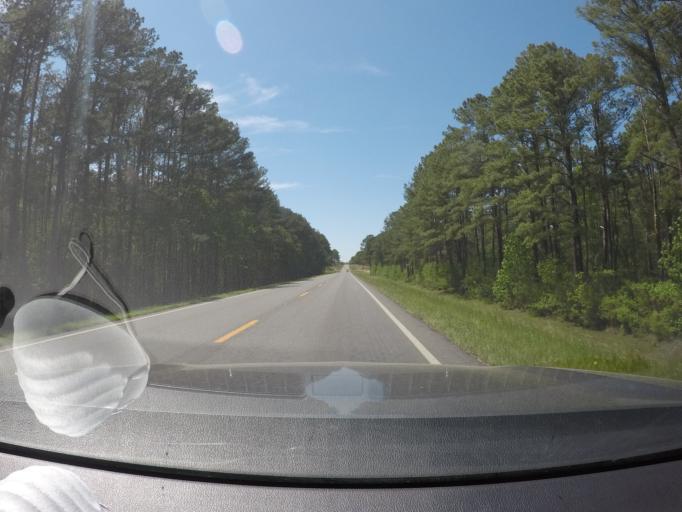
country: US
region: Georgia
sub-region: Evans County
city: Claxton
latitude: 32.1495
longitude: -81.7887
